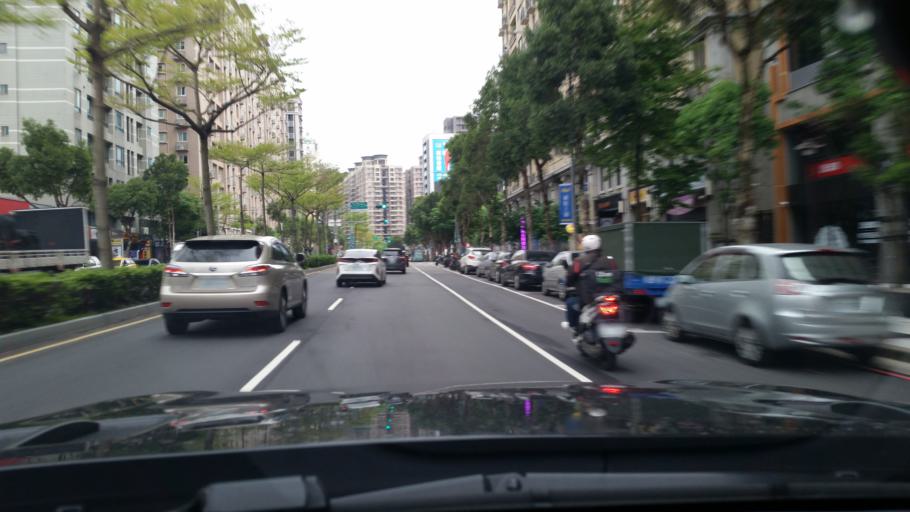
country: TW
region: Taiwan
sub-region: Taoyuan
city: Taoyuan
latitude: 25.0750
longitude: 121.3696
